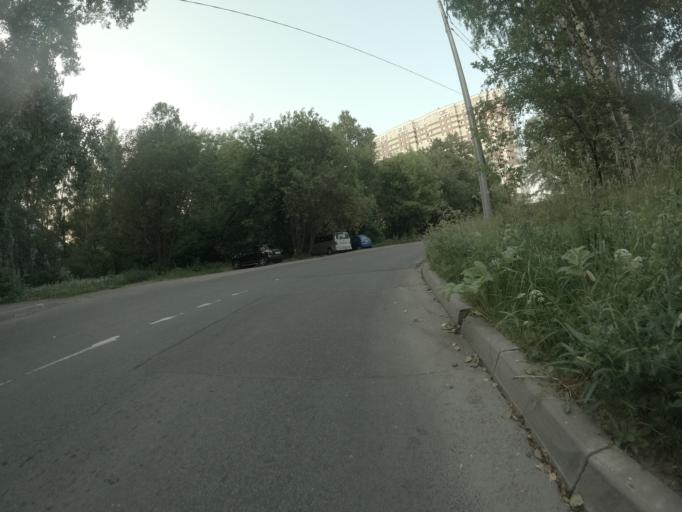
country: RU
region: St.-Petersburg
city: Krasnogvargeisky
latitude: 59.9551
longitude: 30.4448
